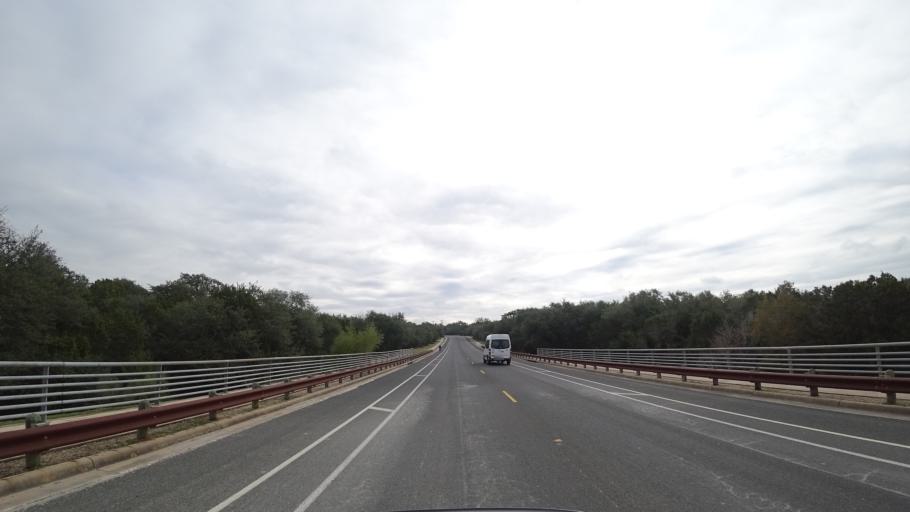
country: US
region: Texas
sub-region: Travis County
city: Shady Hollow
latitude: 30.1960
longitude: -97.8956
